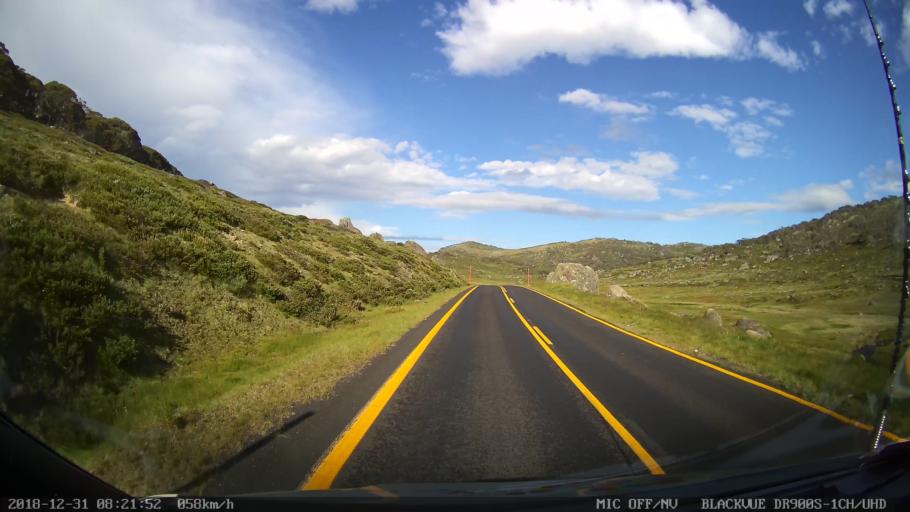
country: AU
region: New South Wales
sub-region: Snowy River
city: Jindabyne
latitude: -36.4288
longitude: 148.3635
